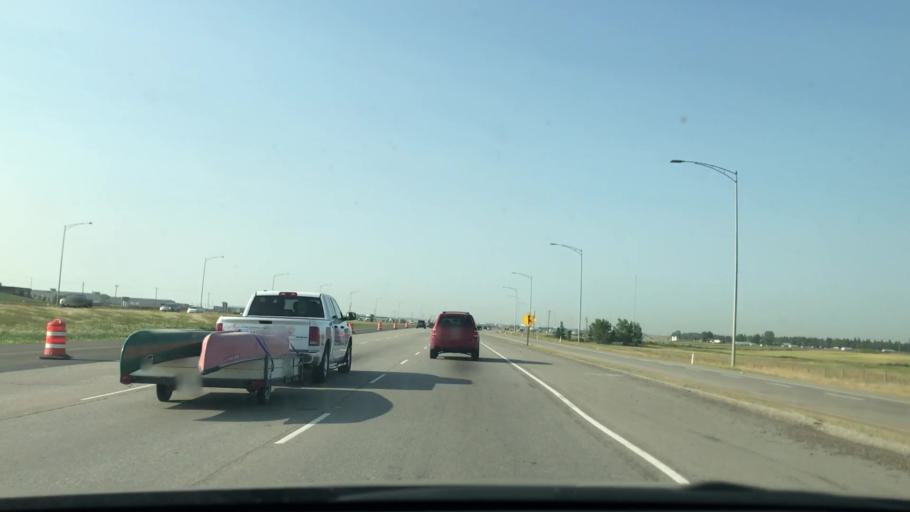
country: CA
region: Alberta
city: Beaumont
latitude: 53.3933
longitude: -113.5144
